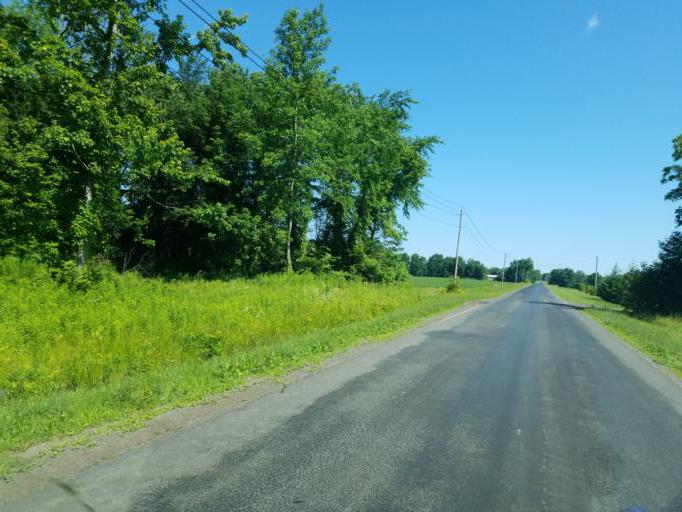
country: US
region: New York
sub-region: Wayne County
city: Wolcott
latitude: 43.1787
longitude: -76.8668
